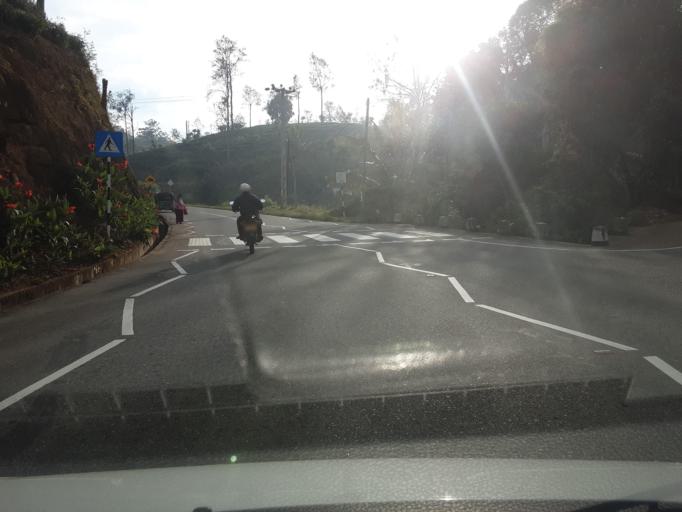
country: LK
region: Uva
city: Badulla
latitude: 6.9308
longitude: 80.9815
